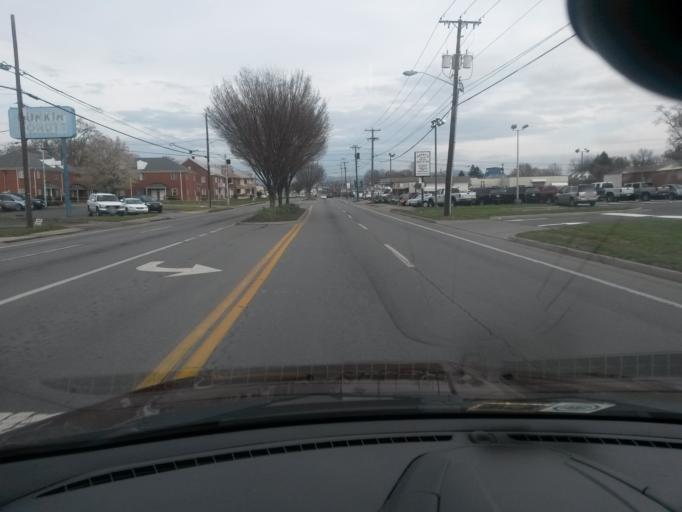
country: US
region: Virginia
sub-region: Roanoke County
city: Hollins
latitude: 37.3108
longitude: -79.9501
